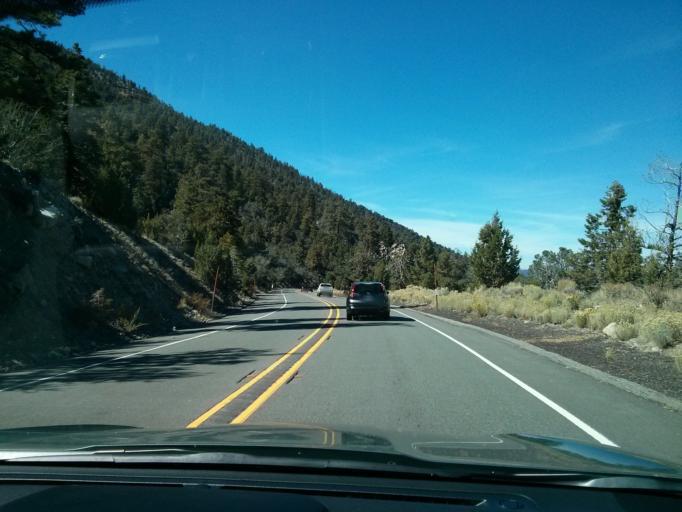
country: US
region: California
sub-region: San Bernardino County
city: Big Bear City
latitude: 34.2071
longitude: -116.7369
